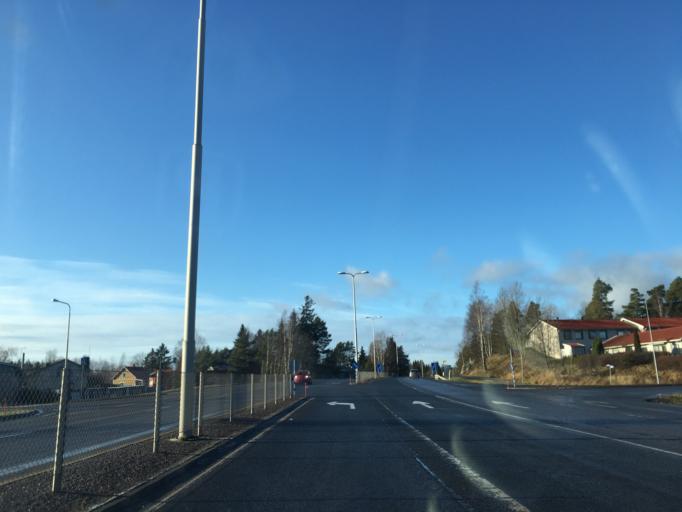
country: FI
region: Varsinais-Suomi
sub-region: Turku
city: Raisio
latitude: 60.4872
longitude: 22.1327
